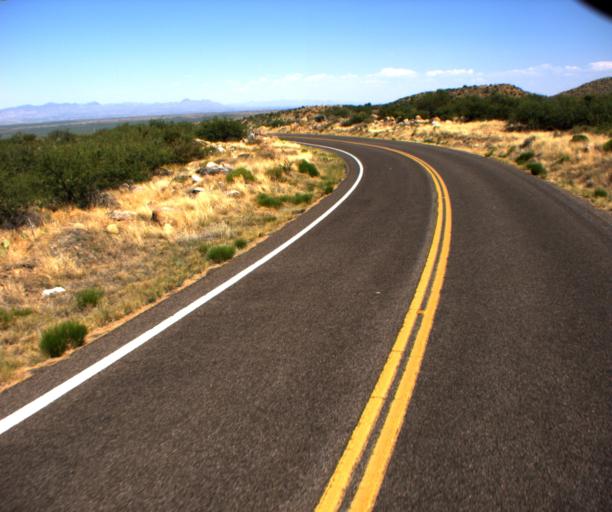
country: US
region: Arizona
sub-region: Graham County
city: Swift Trail Junction
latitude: 32.6869
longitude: -109.7599
